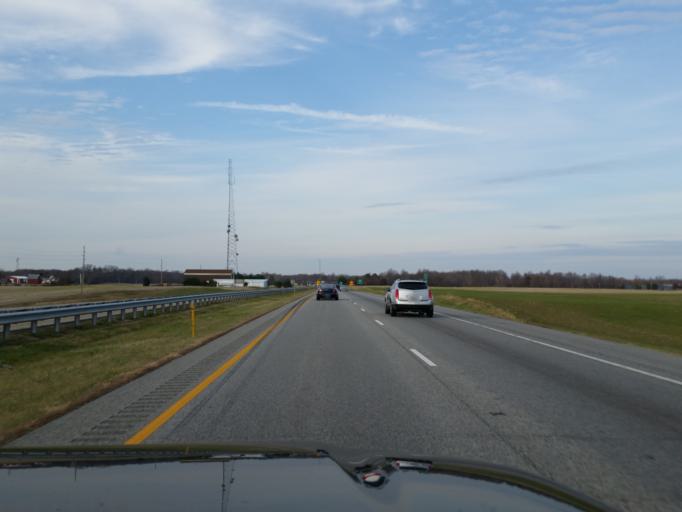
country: US
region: Maryland
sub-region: Queen Anne's County
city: Centreville
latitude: 38.9302
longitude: -76.0623
